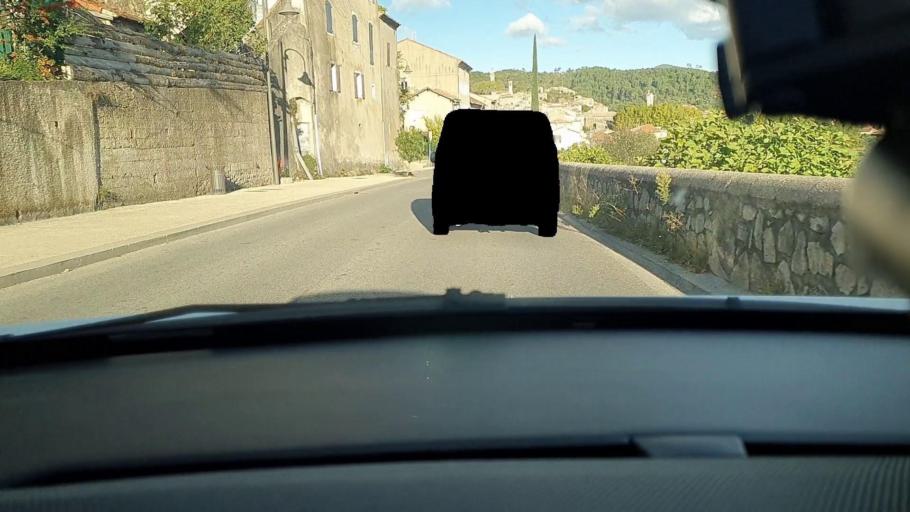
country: FR
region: Languedoc-Roussillon
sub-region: Departement du Gard
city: Saint-Ambroix
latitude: 44.2582
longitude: 4.2037
